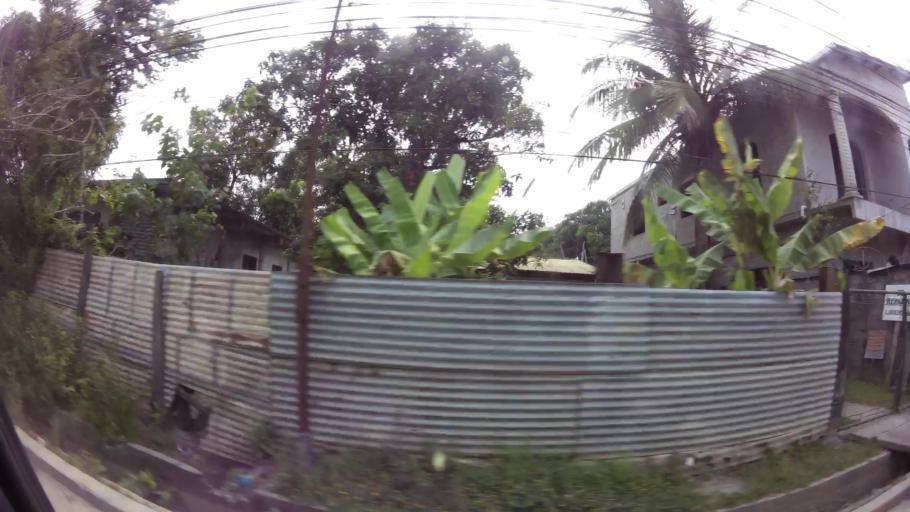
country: HN
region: Atlantida
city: Tela
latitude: 15.7788
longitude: -87.4514
